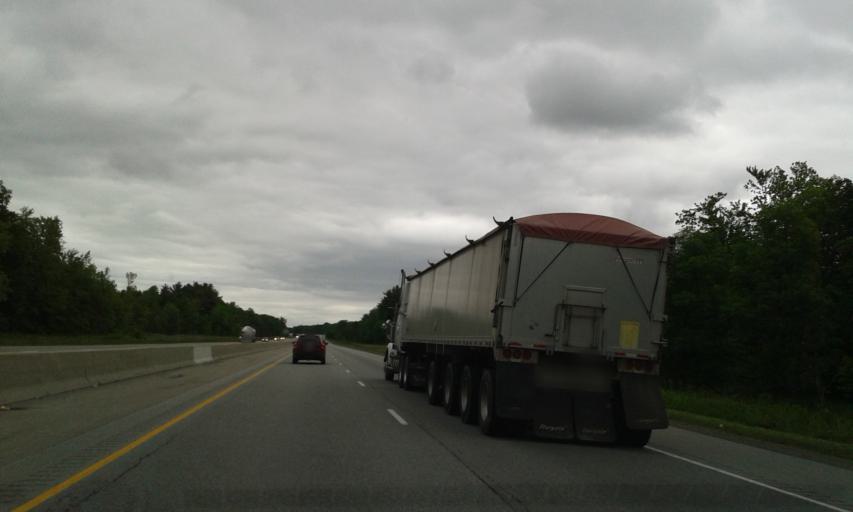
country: CA
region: Ontario
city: Brockville
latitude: 44.5564
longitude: -75.7565
